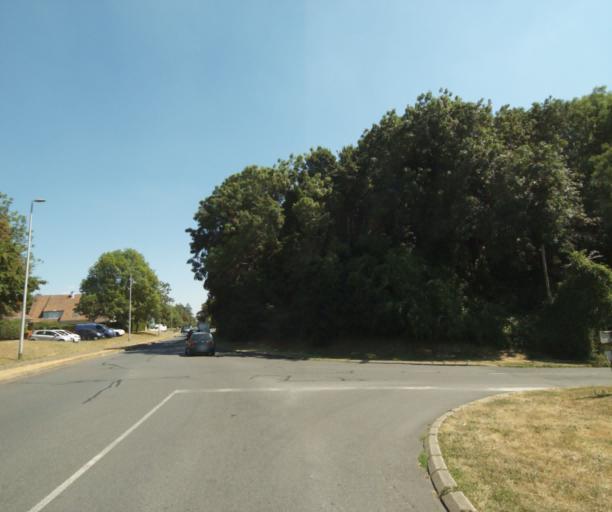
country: FR
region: Ile-de-France
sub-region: Departement de Seine-et-Marne
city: Lagny-sur-Marne
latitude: 48.8653
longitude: 2.7049
